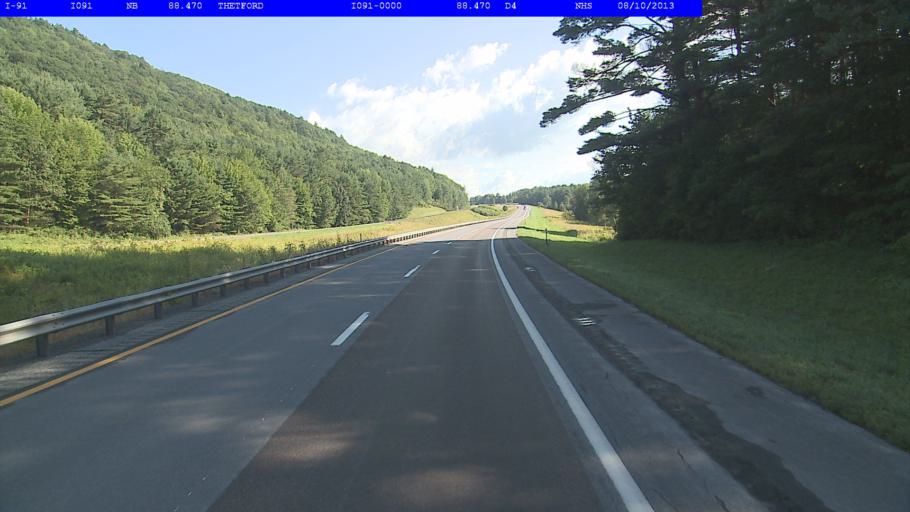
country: US
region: New Hampshire
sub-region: Grafton County
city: Orford
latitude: 43.8700
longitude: -72.1862
